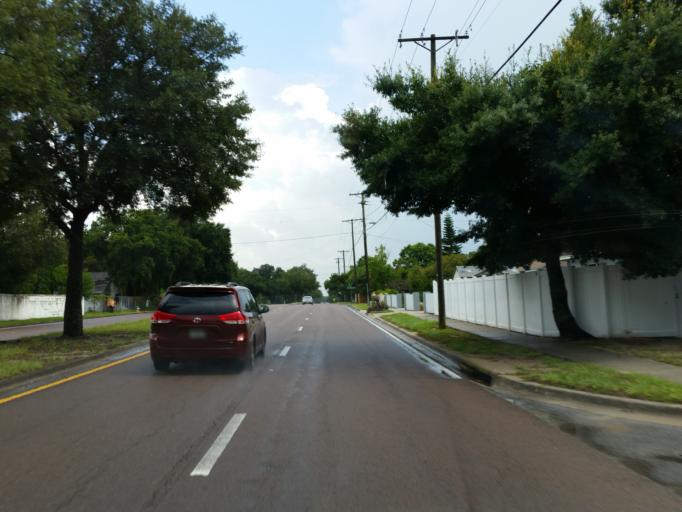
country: US
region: Florida
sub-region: Hillsborough County
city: Brandon
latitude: 27.9118
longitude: -82.2940
